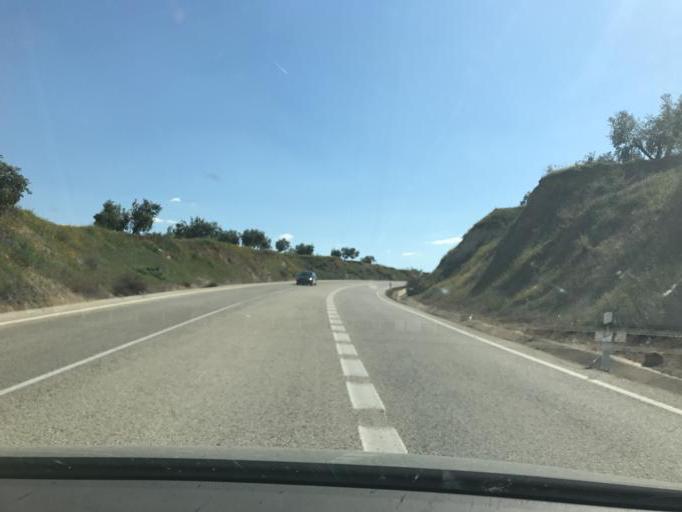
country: ES
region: Andalusia
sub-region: Province of Cordoba
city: Fuente-Tojar
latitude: 37.5783
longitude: -4.1638
